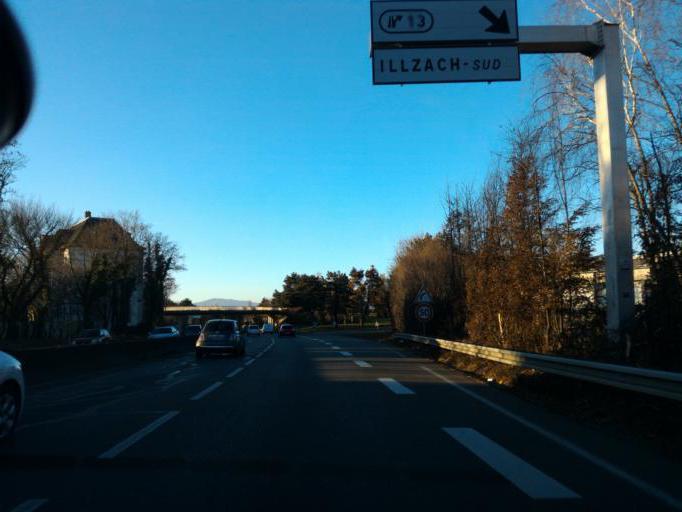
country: FR
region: Alsace
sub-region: Departement du Haut-Rhin
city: Illzach
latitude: 47.7641
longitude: 7.3494
